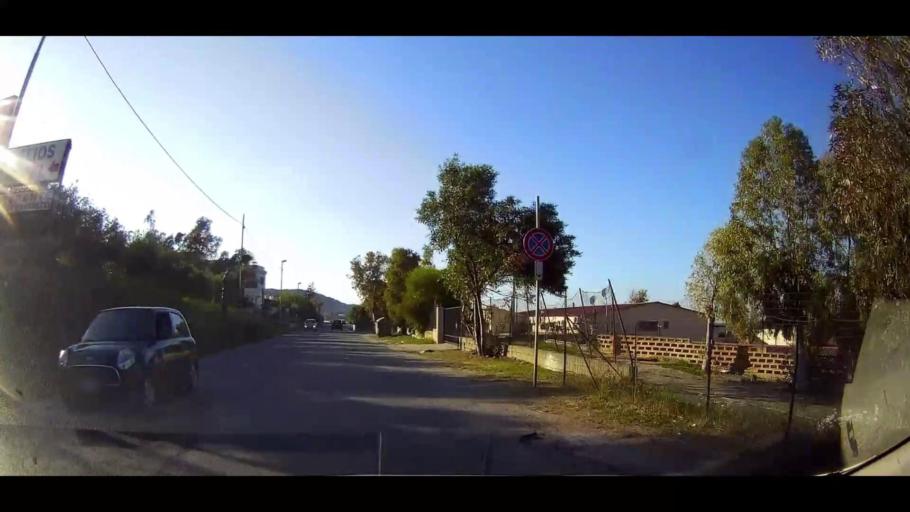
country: IT
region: Calabria
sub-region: Provincia di Crotone
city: Crotone
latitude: 39.0532
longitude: 17.1389
